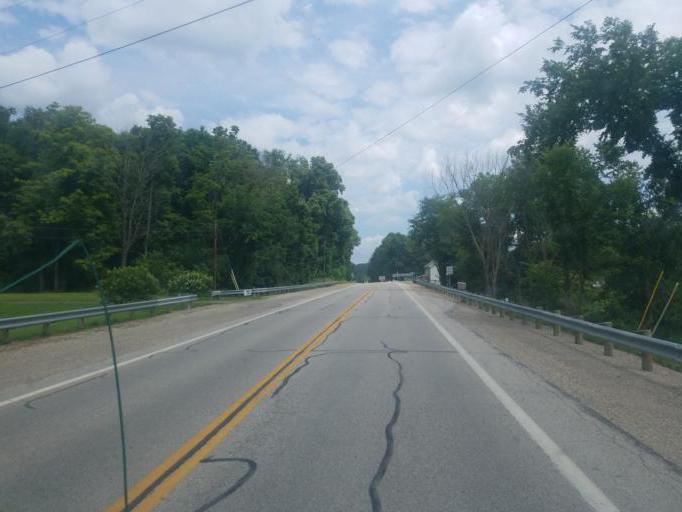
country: US
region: Ohio
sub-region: Perry County
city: Thornport
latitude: 39.9558
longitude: -82.3475
